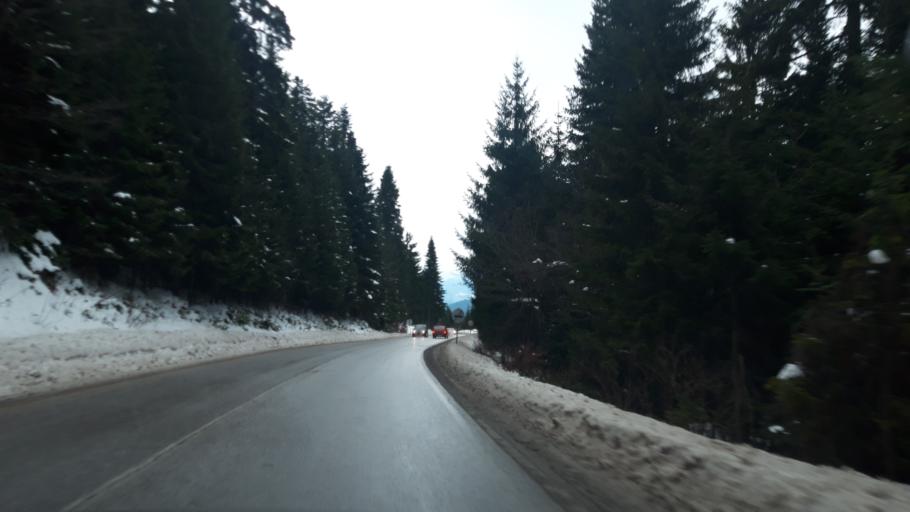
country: BA
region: Republika Srpska
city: Pale
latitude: 43.9159
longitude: 18.6486
